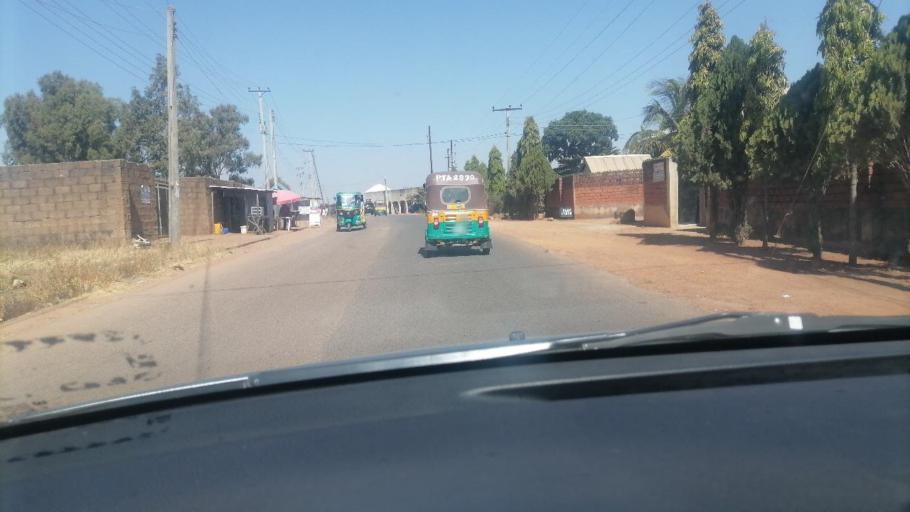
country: NG
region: Plateau
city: Jos
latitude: 9.8705
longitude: 8.9065
